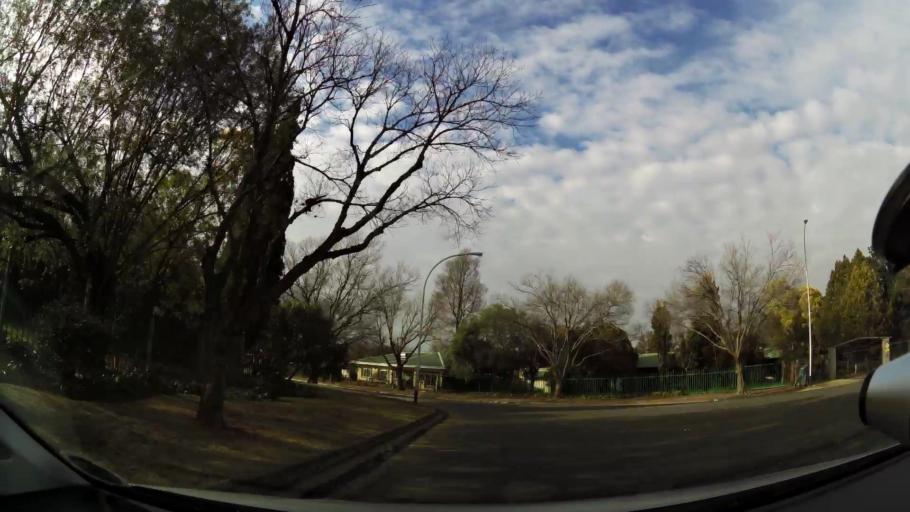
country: ZA
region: Orange Free State
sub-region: Mangaung Metropolitan Municipality
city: Bloemfontein
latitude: -29.1225
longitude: 26.1763
